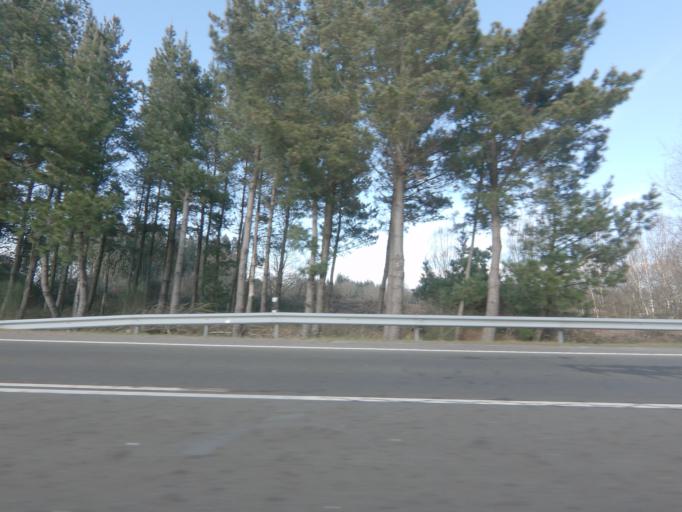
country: ES
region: Galicia
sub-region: Provincia da Coruna
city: Ribeira
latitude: 42.7097
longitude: -8.3516
